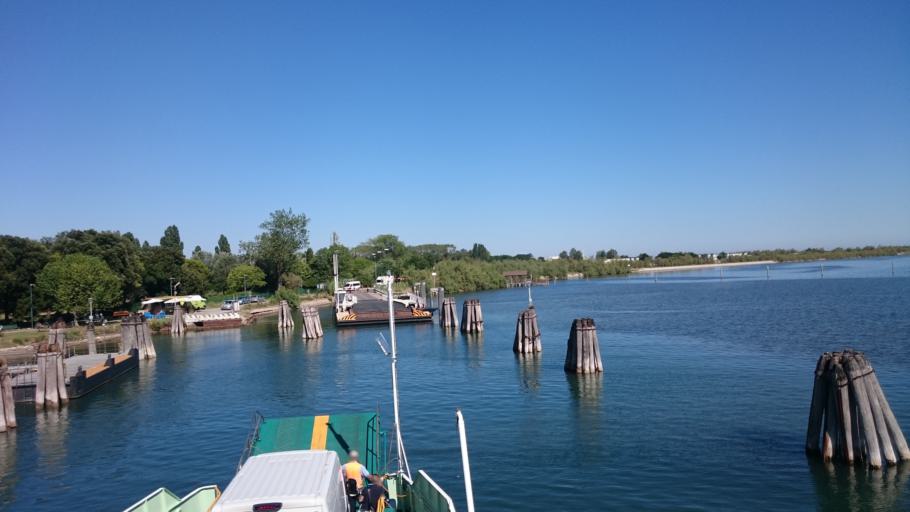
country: IT
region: Veneto
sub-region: Provincia di Venezia
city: San Pietro in Volta
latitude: 45.3329
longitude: 12.3160
